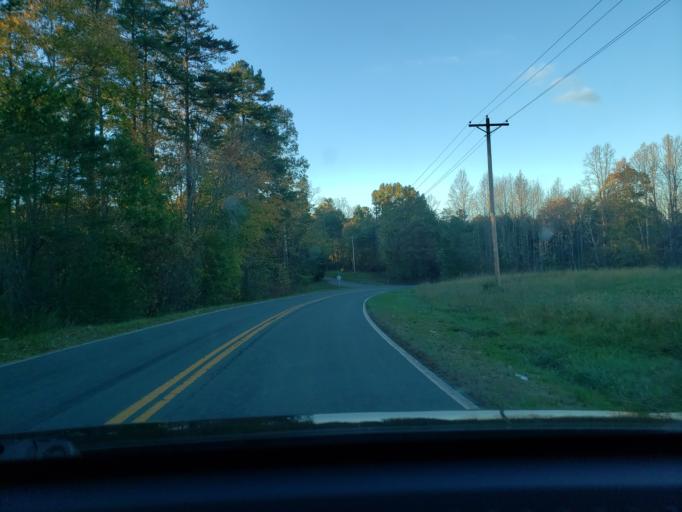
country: US
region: North Carolina
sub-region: Stokes County
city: Danbury
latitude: 36.3778
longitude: -80.1883
